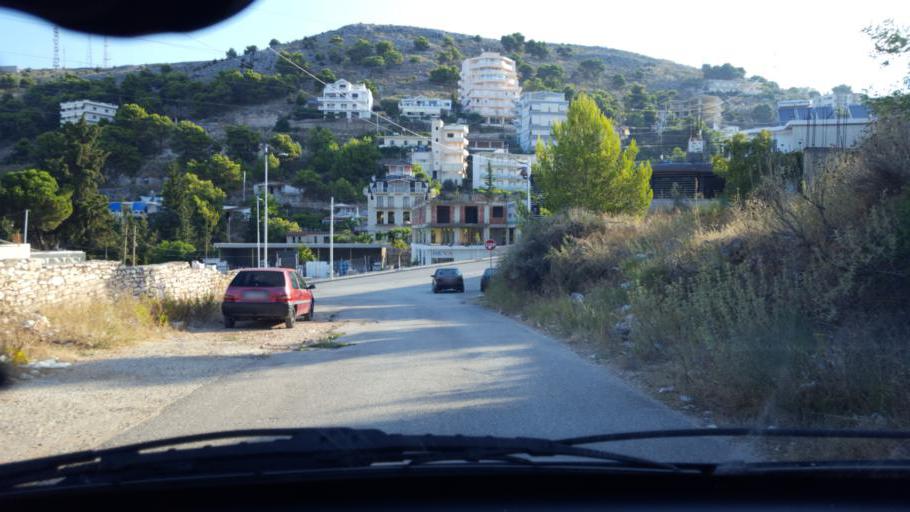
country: AL
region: Vlore
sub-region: Rrethi i Sarandes
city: Sarande
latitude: 39.8681
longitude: 20.0196
